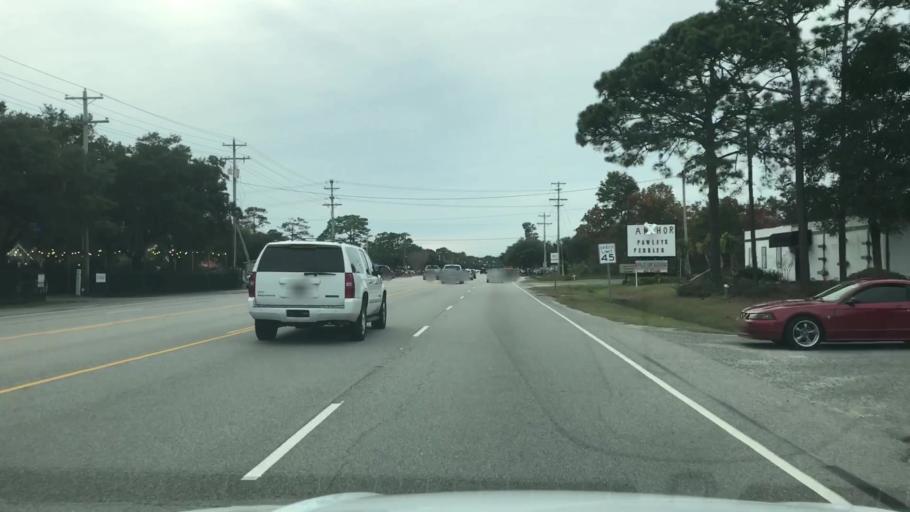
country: US
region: South Carolina
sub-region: Georgetown County
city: Murrells Inlet
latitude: 33.4322
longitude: -79.1412
